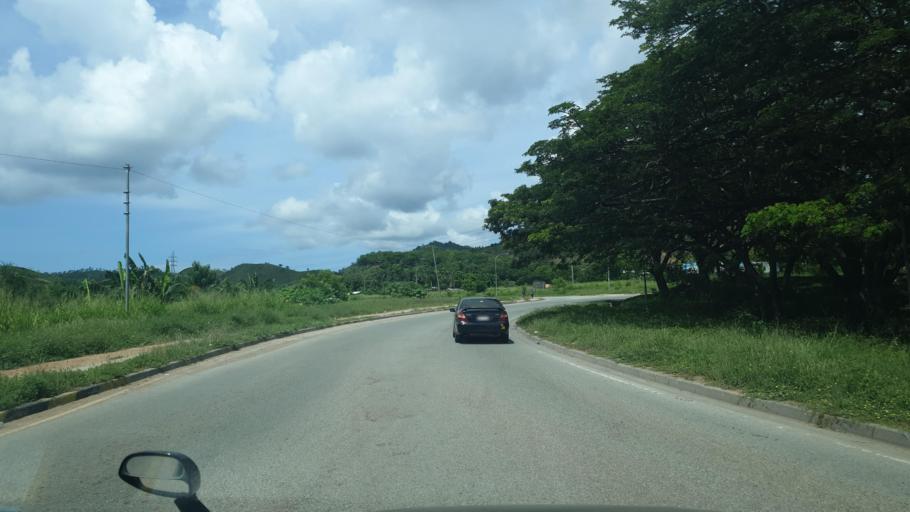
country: PG
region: National Capital
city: Port Moresby
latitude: -9.3983
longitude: 147.1593
